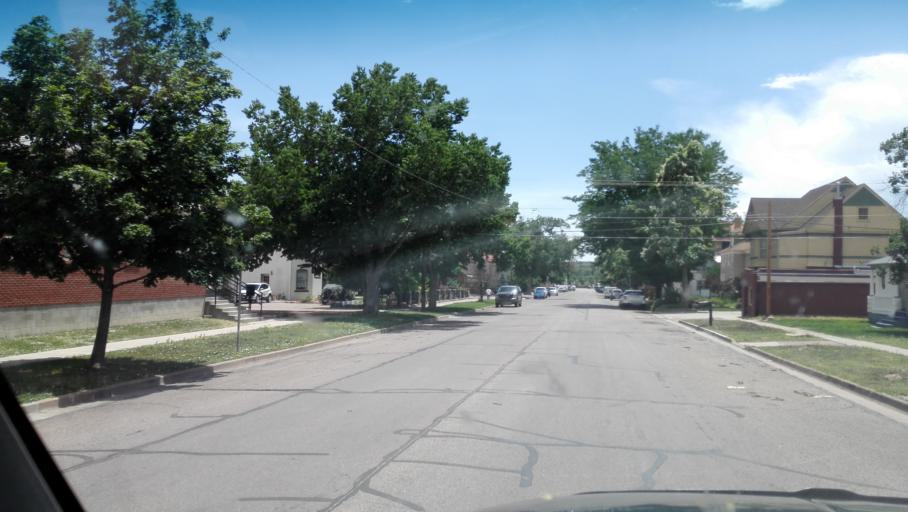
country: US
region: Colorado
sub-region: Fremont County
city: Canon City
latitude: 38.4429
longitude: -105.2426
